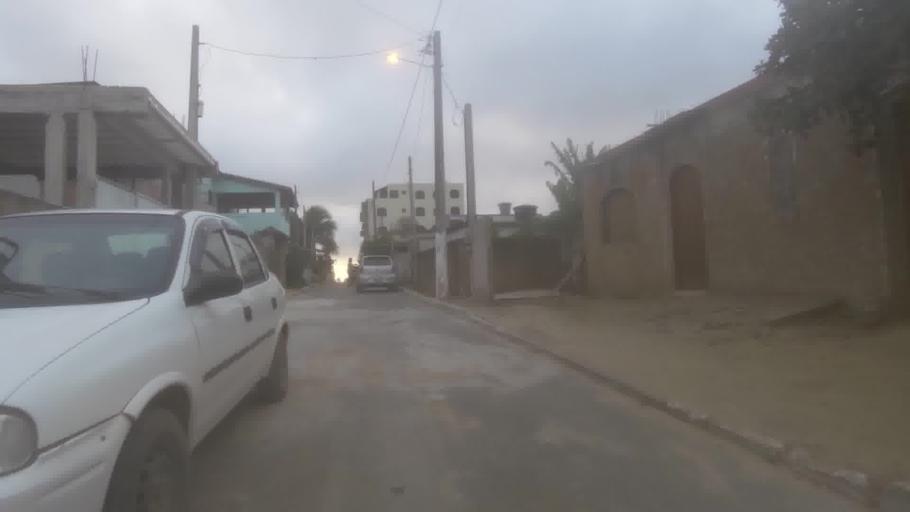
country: BR
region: Espirito Santo
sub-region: Marataizes
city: Marataizes
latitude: -21.0415
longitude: -40.8293
